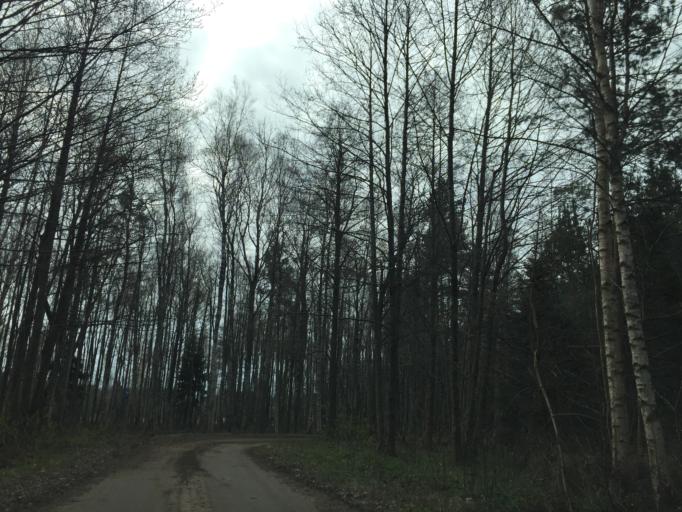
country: LV
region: Salacgrivas
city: Salacgriva
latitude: 57.5414
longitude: 24.3676
